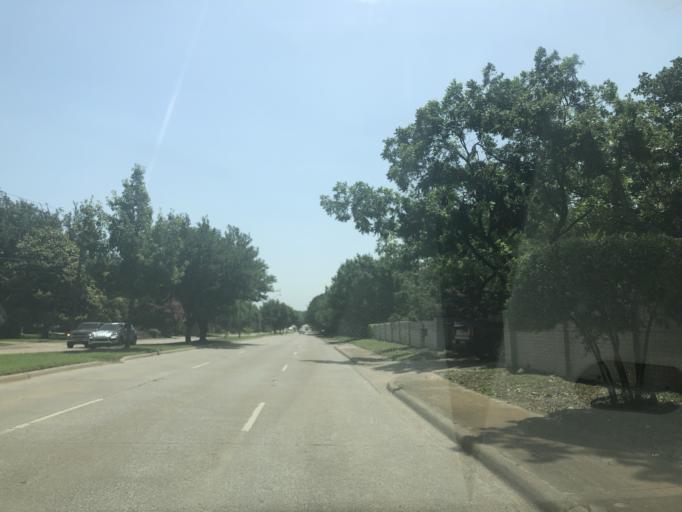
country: US
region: Texas
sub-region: Dallas County
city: University Park
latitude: 32.8801
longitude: -96.8319
